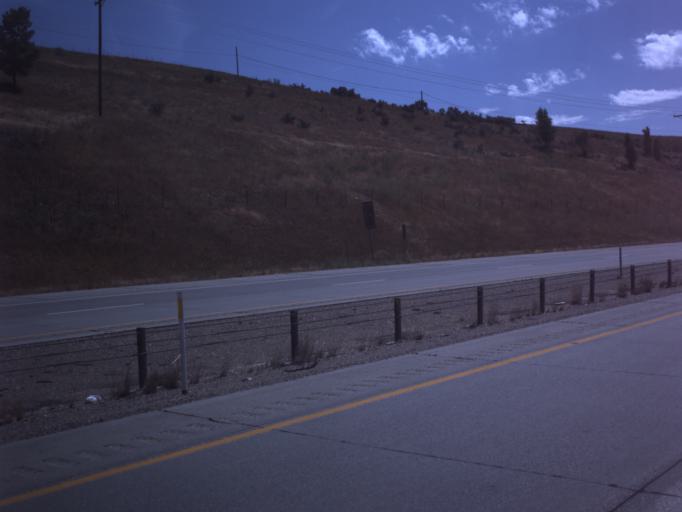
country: US
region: Utah
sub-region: Morgan County
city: Mountain Green
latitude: 41.1234
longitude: -111.7656
